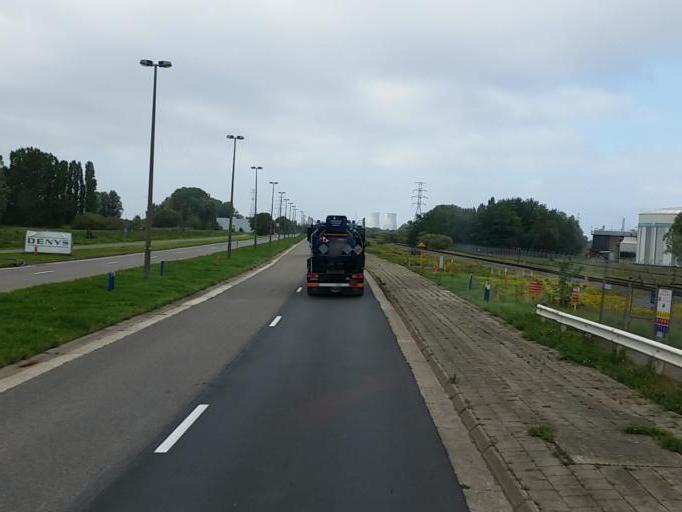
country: BE
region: Flanders
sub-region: Provincie Antwerpen
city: Stabroek
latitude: 51.2954
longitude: 4.3175
